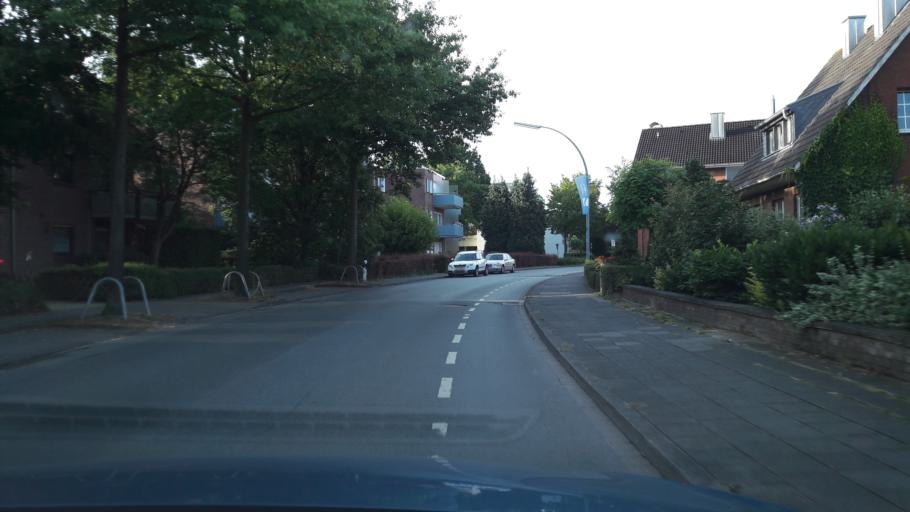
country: DE
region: North Rhine-Westphalia
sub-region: Regierungsbezirk Munster
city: Everswinkel
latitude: 51.9237
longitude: 7.8491
